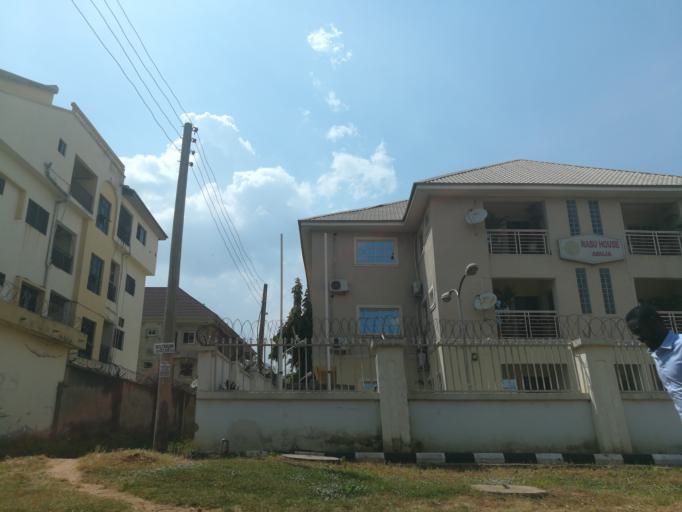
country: NG
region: Abuja Federal Capital Territory
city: Abuja
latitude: 9.0496
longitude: 7.4464
